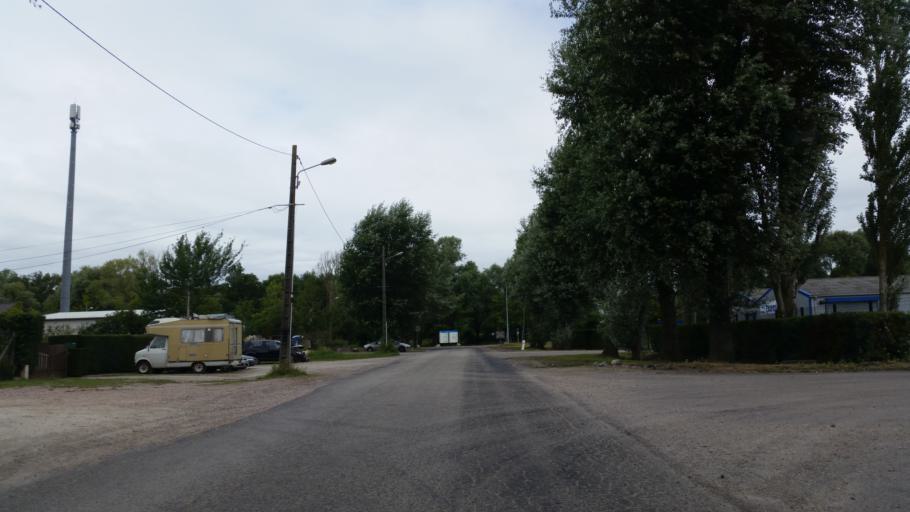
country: FR
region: Lower Normandy
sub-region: Departement du Calvados
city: La Riviere-Saint-Sauveur
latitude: 49.4244
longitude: 0.2599
